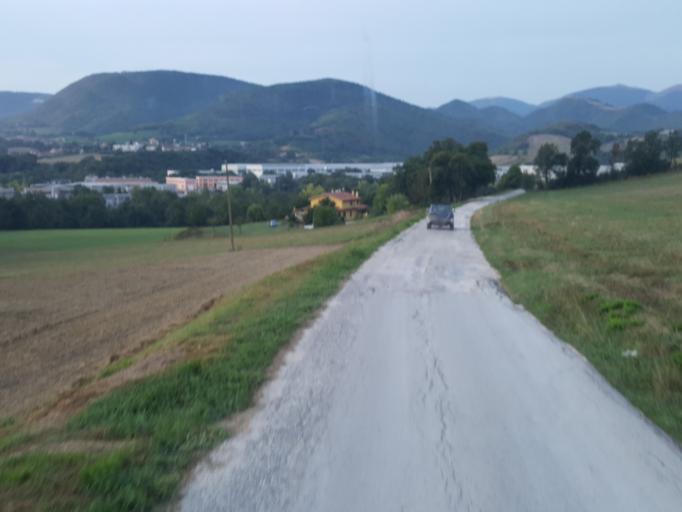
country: IT
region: The Marches
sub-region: Provincia di Ancona
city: Fabriano
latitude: 43.3519
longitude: 12.8654
